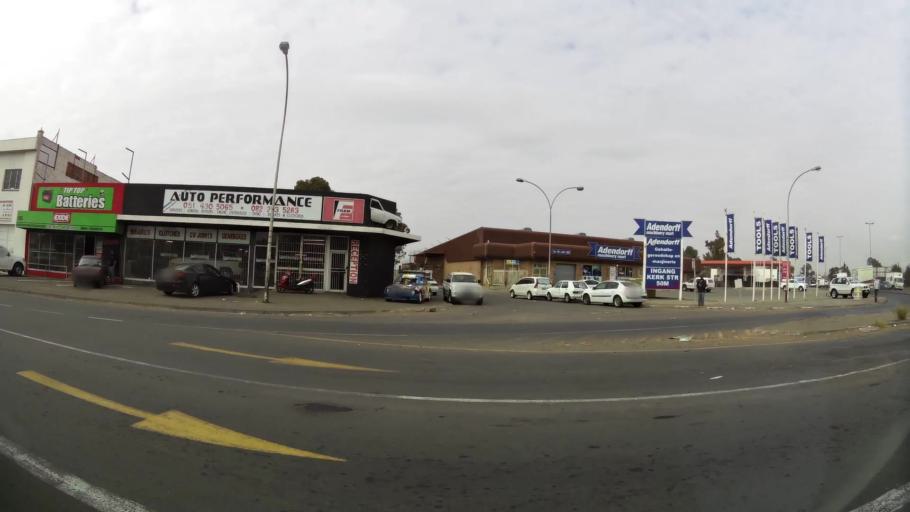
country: ZA
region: Orange Free State
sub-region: Mangaung Metropolitan Municipality
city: Bloemfontein
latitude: -29.1362
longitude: 26.2171
